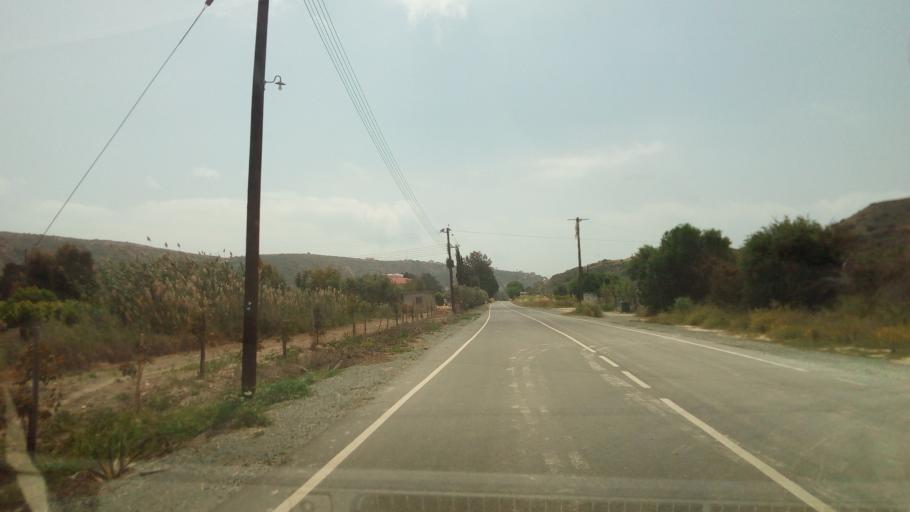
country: CY
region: Limassol
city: Pissouri
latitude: 34.6684
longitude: 32.7264
